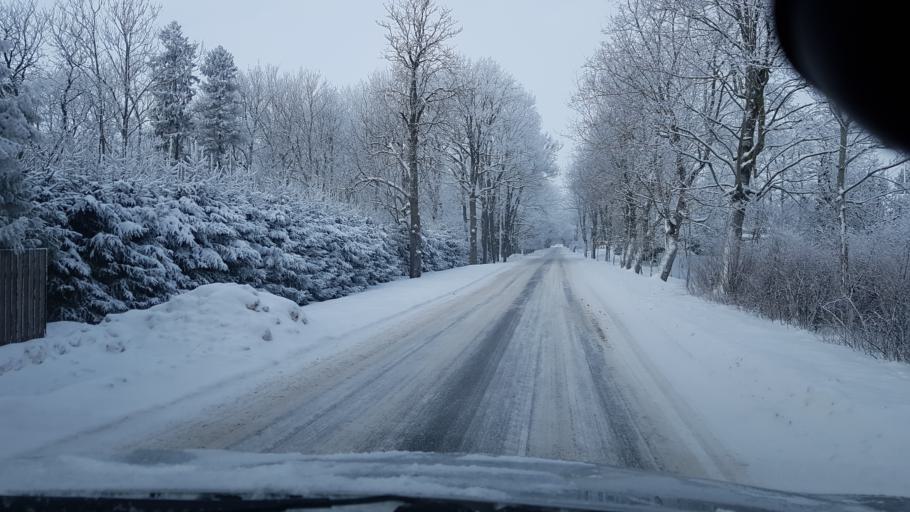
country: EE
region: Harju
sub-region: Keila linn
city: Keila
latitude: 59.3245
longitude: 24.4508
